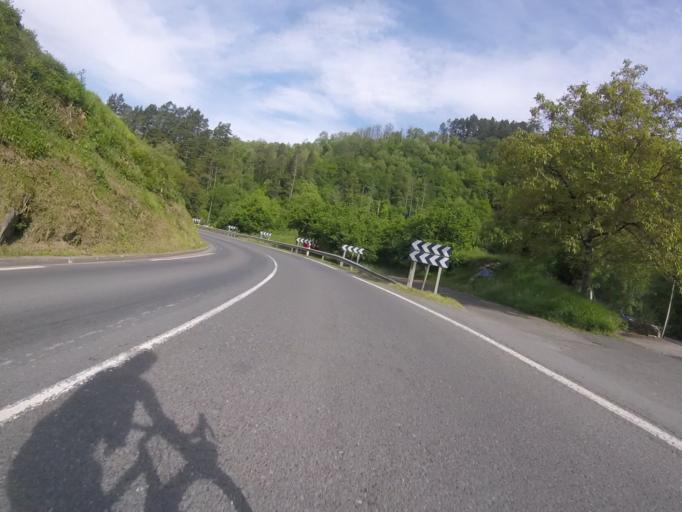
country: ES
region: Basque Country
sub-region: Provincia de Guipuzcoa
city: Urretxu
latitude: 43.1127
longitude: -2.3237
